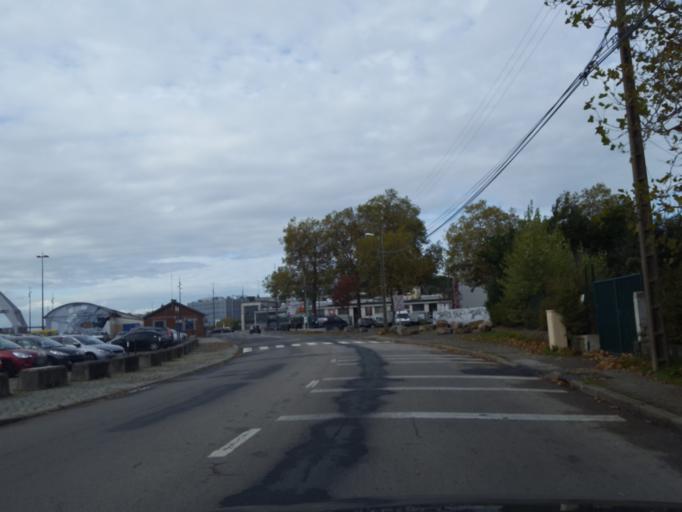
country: FR
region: Pays de la Loire
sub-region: Departement de la Loire-Atlantique
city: Nantes
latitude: 47.1997
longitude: -1.5713
